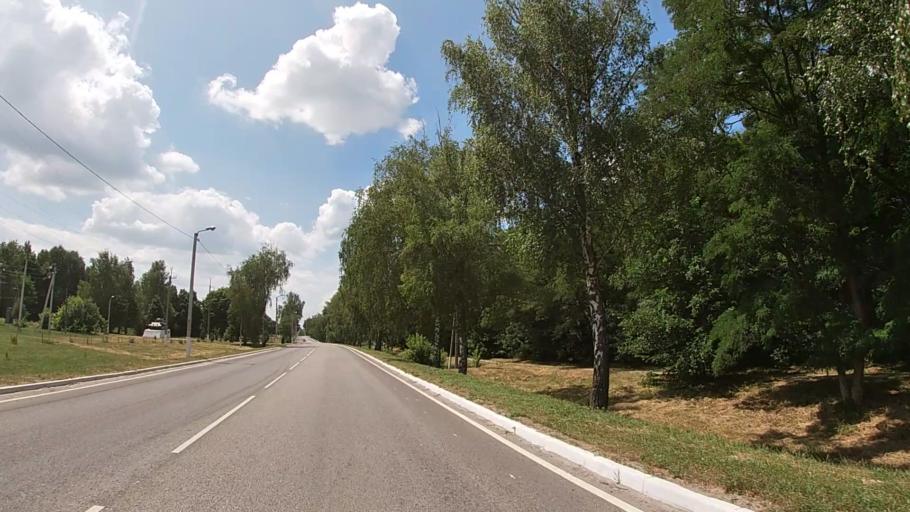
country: RU
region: Belgorod
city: Grayvoron
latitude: 50.4893
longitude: 35.6943
